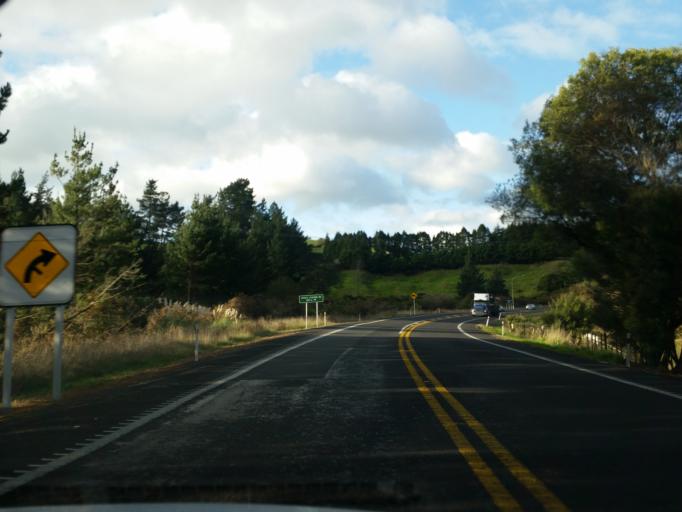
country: NZ
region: Bay of Plenty
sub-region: Western Bay of Plenty District
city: Katikati
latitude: -37.6493
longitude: 175.9735
